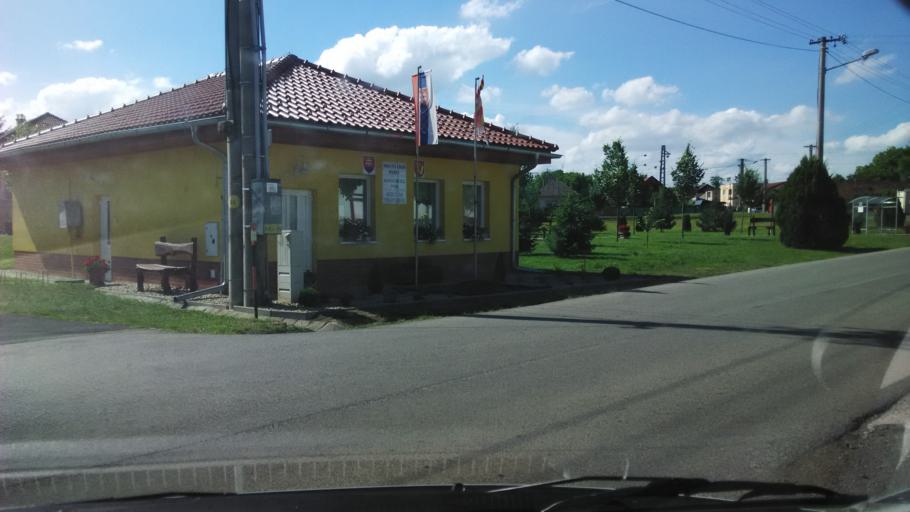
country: SK
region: Nitriansky
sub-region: Okres Nitra
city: Vrable
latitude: 48.1144
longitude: 18.3878
